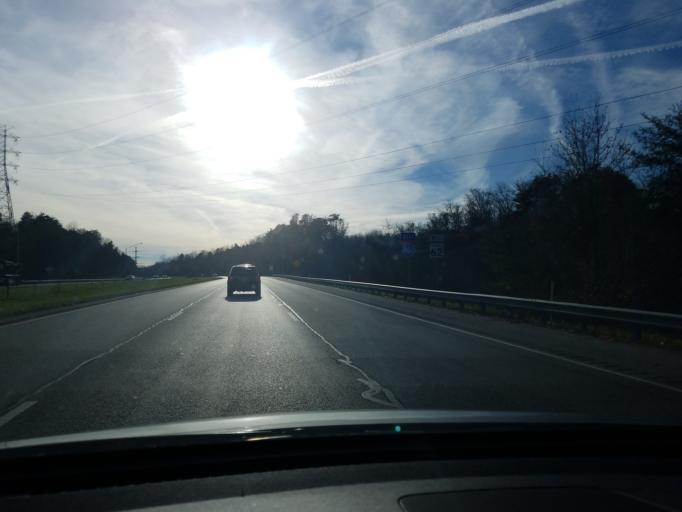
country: US
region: Indiana
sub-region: Floyd County
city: New Albany
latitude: 38.3101
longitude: -85.8469
